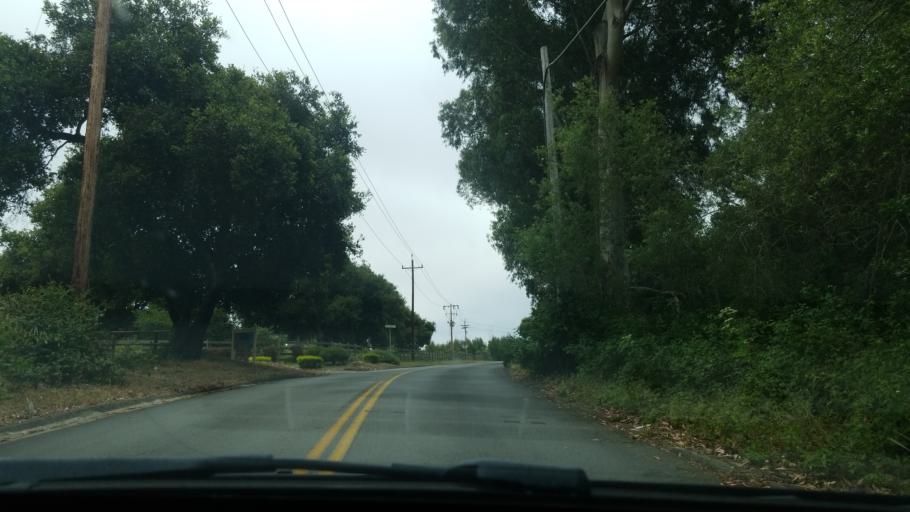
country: US
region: California
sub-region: San Luis Obispo County
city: Callender
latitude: 35.0748
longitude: -120.5420
